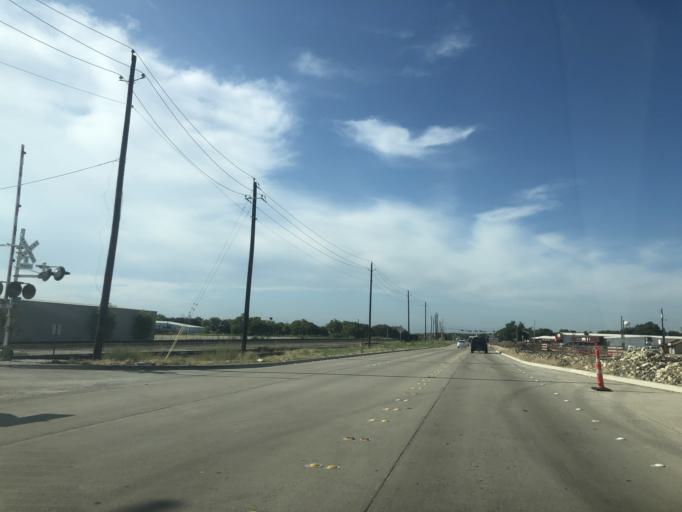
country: US
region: Texas
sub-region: Denton County
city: Justin
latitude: 33.0877
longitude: -97.2954
